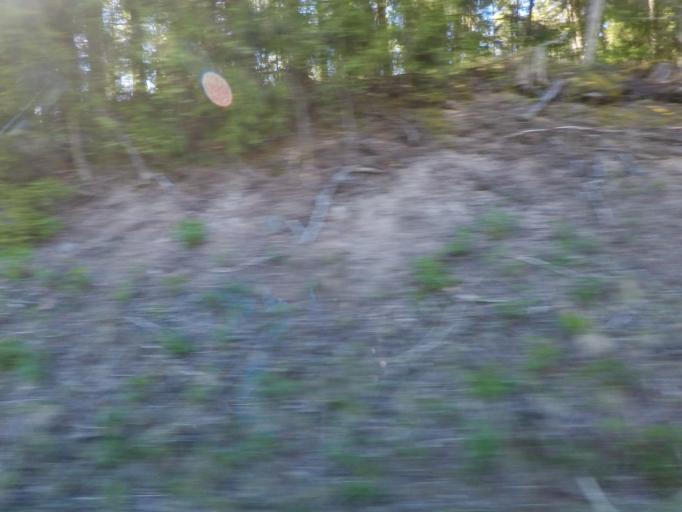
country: FI
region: Uusimaa
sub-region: Helsinki
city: Sammatti
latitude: 60.3487
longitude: 23.7998
